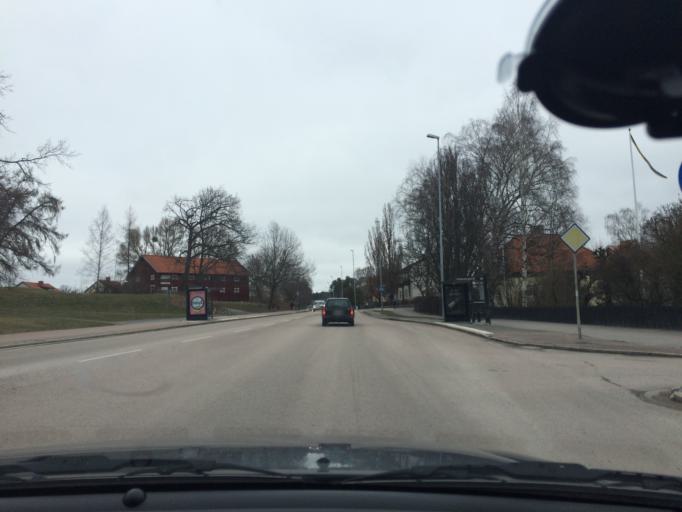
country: SE
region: Vaestmanland
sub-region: Vasteras
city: Vasteras
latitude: 59.6196
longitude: 16.5448
